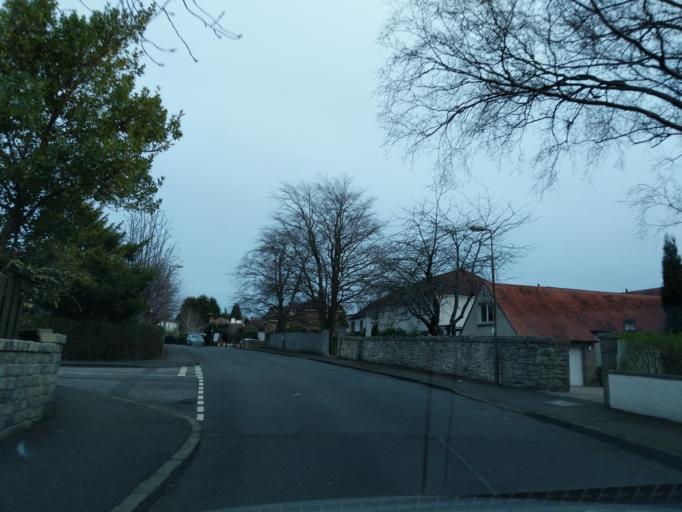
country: GB
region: Scotland
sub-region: Edinburgh
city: Currie
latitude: 55.9668
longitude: -3.3121
